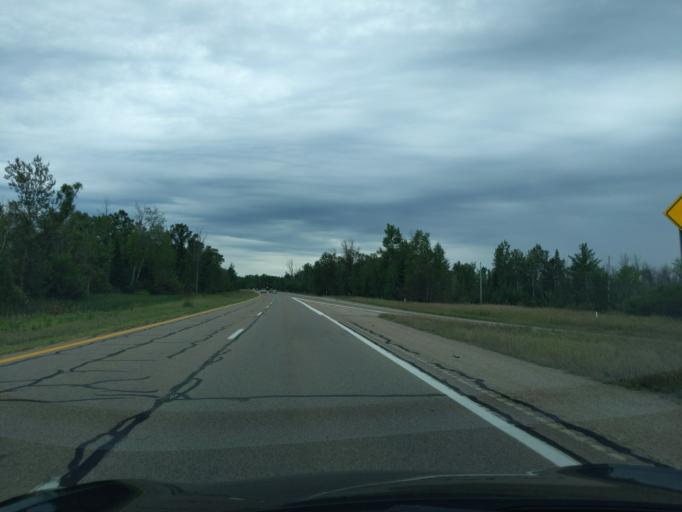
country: US
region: Michigan
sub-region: Roscommon County
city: Houghton Lake
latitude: 44.2672
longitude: -84.8033
